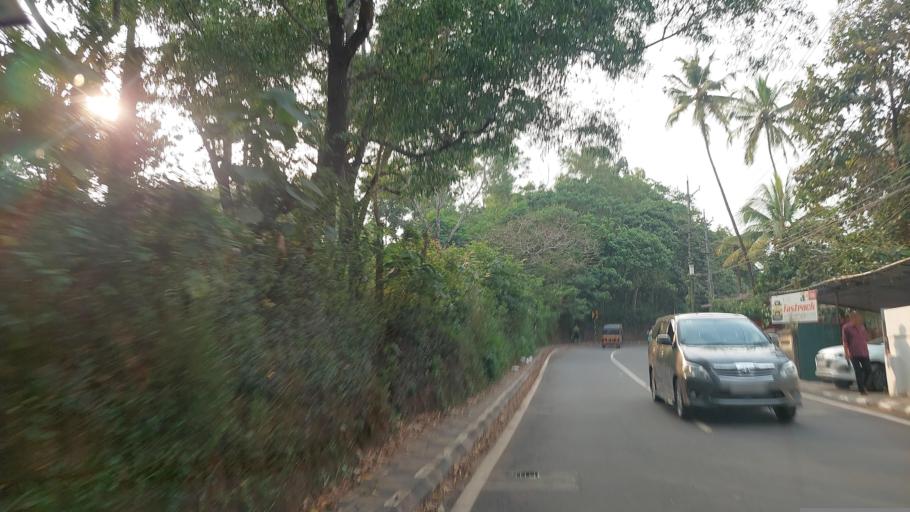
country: IN
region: Kerala
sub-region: Kozhikode
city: Kozhikode
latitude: 11.2904
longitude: 75.7735
